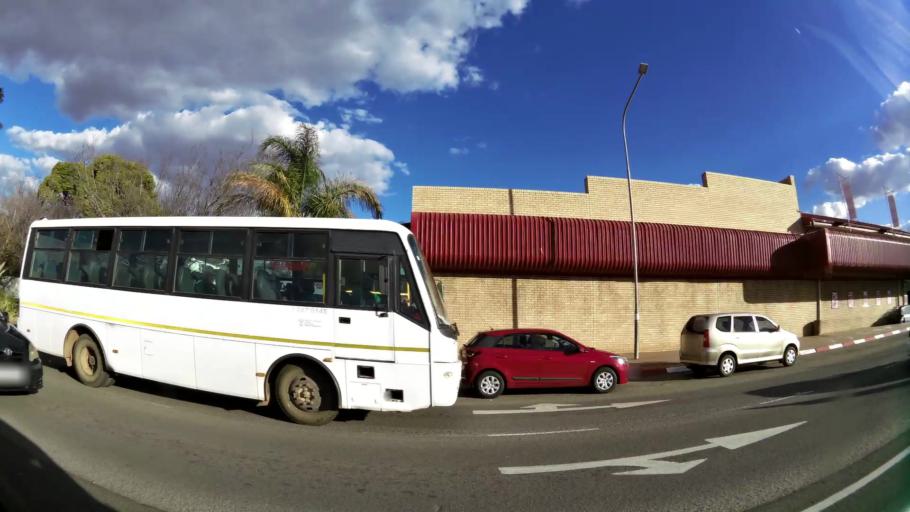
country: ZA
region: North-West
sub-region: Dr Kenneth Kaunda District Municipality
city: Potchefstroom
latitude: -26.7000
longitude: 27.0893
